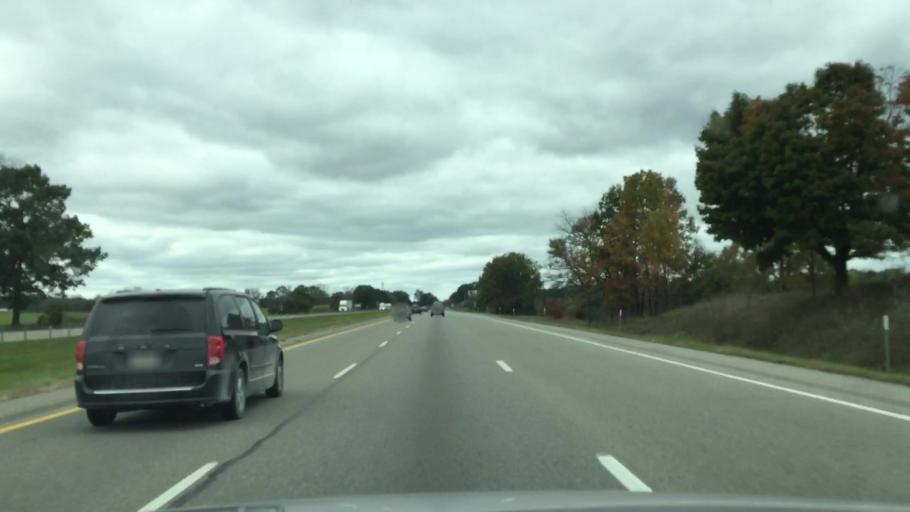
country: US
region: Michigan
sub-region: Calhoun County
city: Lakeview
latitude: 42.2653
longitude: -85.2417
